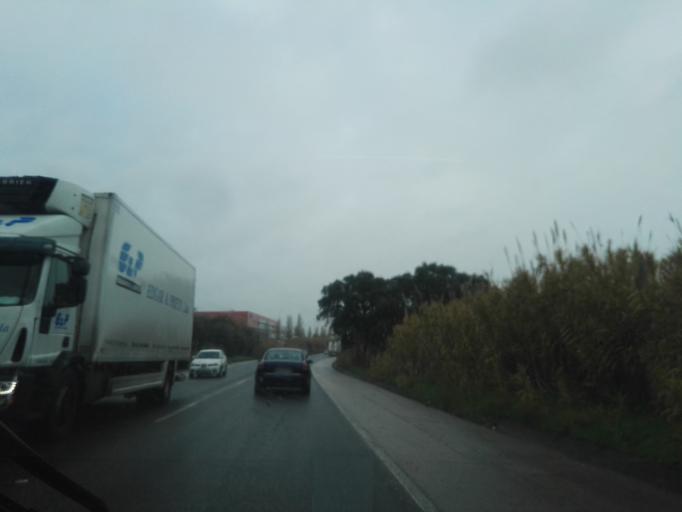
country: PT
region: Lisbon
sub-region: Alenquer
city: Carregado
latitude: 39.0417
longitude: -8.9279
